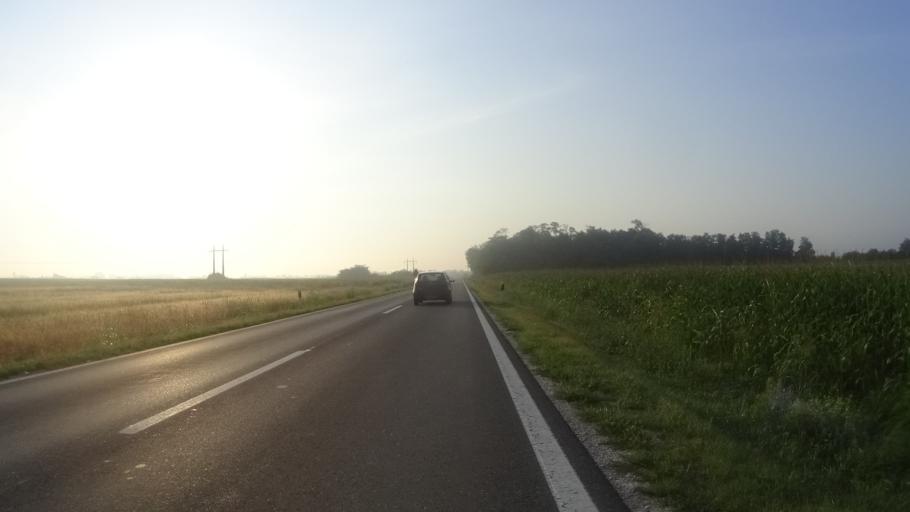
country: HR
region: Varazdinska
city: Petrijanec
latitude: 46.3509
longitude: 16.2000
